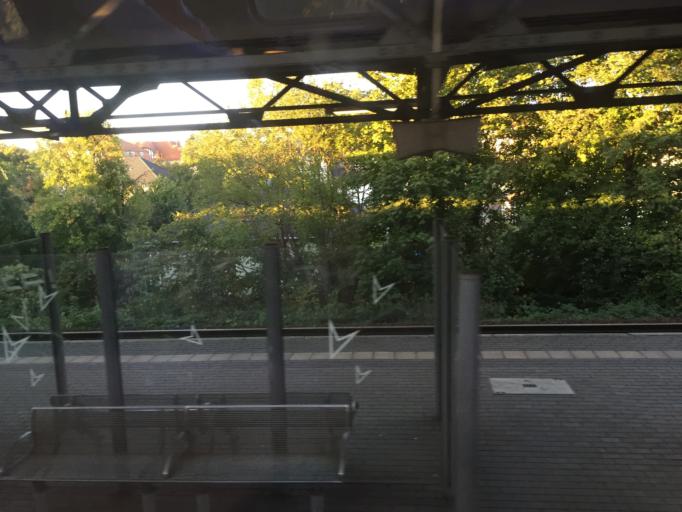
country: DE
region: Saxony
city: Dresden
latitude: 51.0306
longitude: 13.7620
